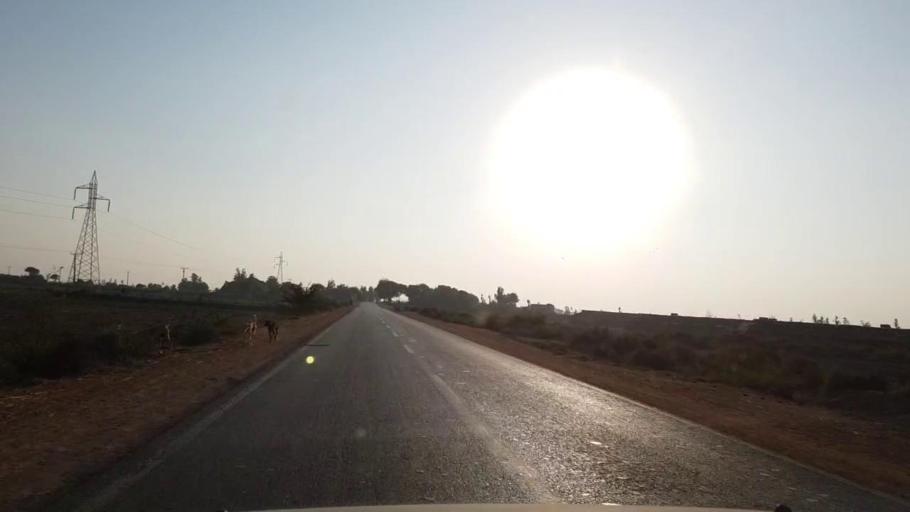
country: PK
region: Sindh
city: Daro Mehar
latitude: 24.6433
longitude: 68.1196
